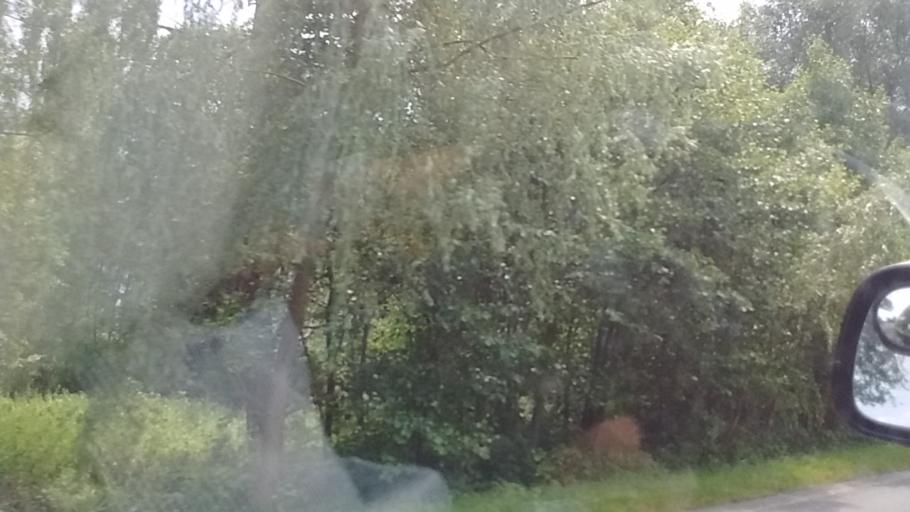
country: PL
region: Subcarpathian Voivodeship
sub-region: Powiat lezajski
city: Brzoza Krolewska
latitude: 50.1968
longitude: 22.3473
